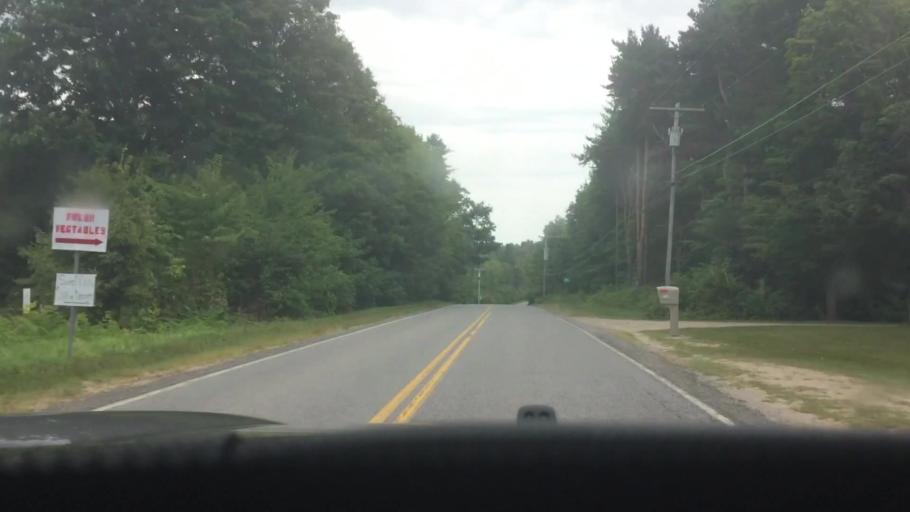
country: US
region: New York
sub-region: St. Lawrence County
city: Hannawa Falls
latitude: 44.6138
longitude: -74.8733
